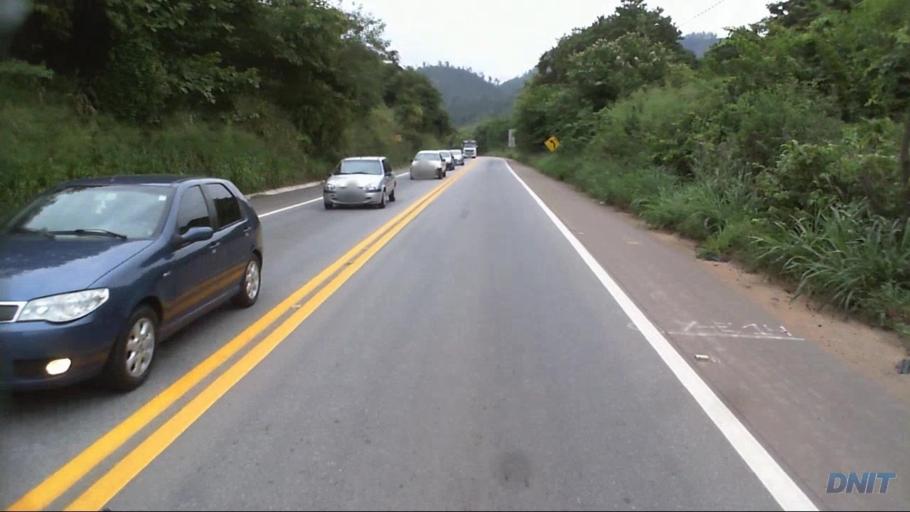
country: BR
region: Minas Gerais
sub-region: Timoteo
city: Timoteo
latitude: -19.5489
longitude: -42.6988
